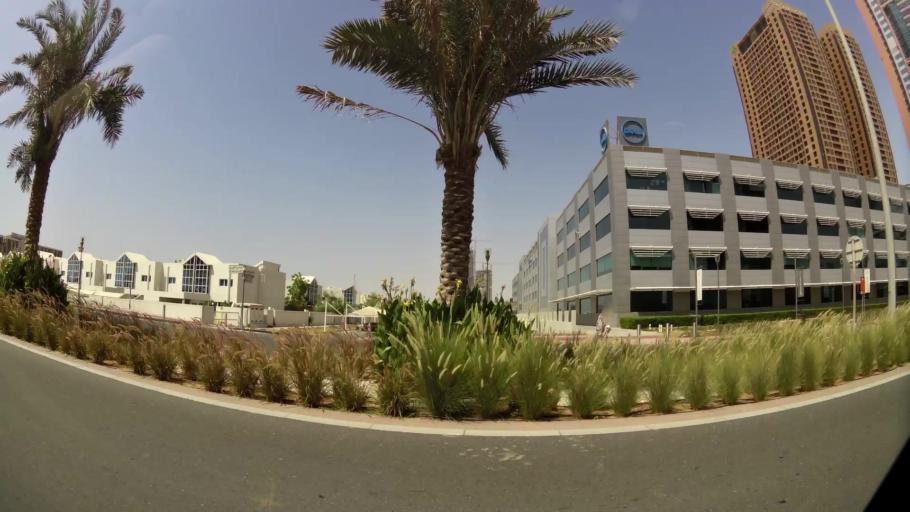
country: AE
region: Dubai
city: Dubai
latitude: 25.1031
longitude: 55.1698
